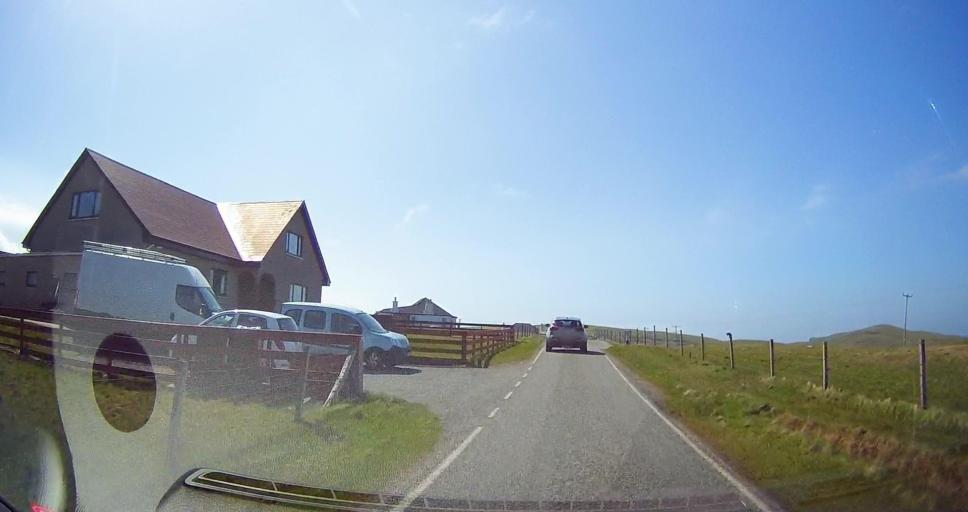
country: GB
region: Scotland
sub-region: Shetland Islands
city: Sandwick
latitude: 60.0856
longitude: -1.3313
